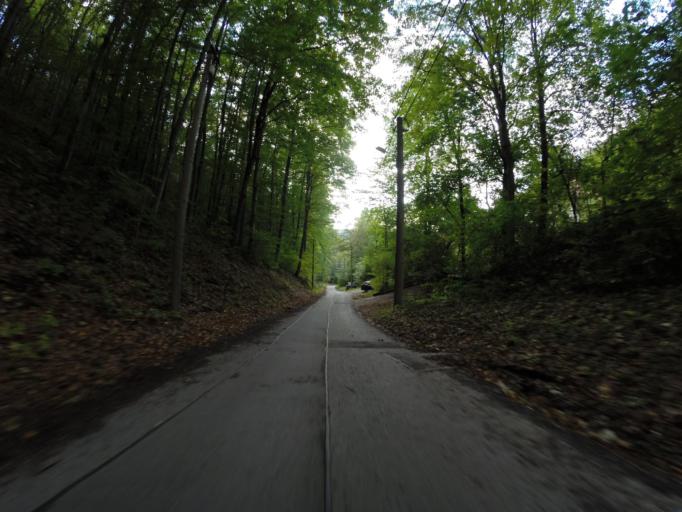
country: DE
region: Thuringia
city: Jena
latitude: 50.9418
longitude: 11.5653
